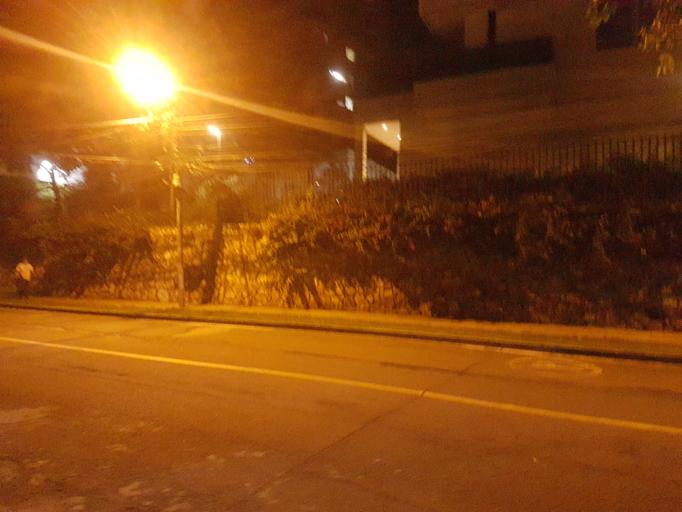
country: CO
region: Valle del Cauca
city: Cali
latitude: 3.4526
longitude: -76.5451
